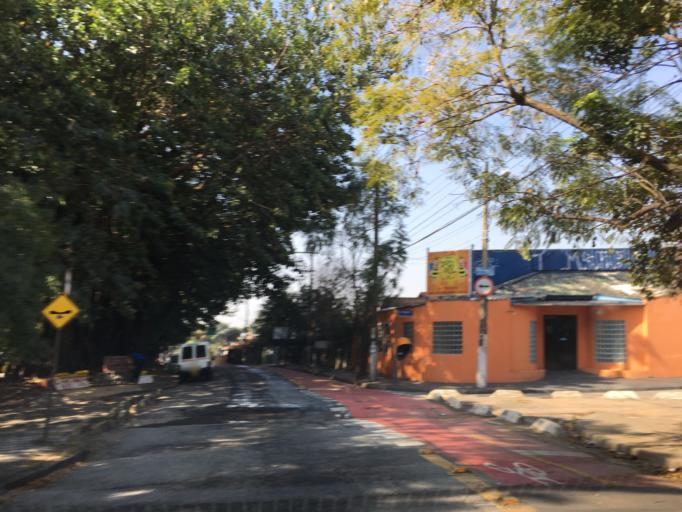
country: BR
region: Sao Paulo
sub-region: Osasco
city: Osasco
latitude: -23.5773
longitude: -46.7224
